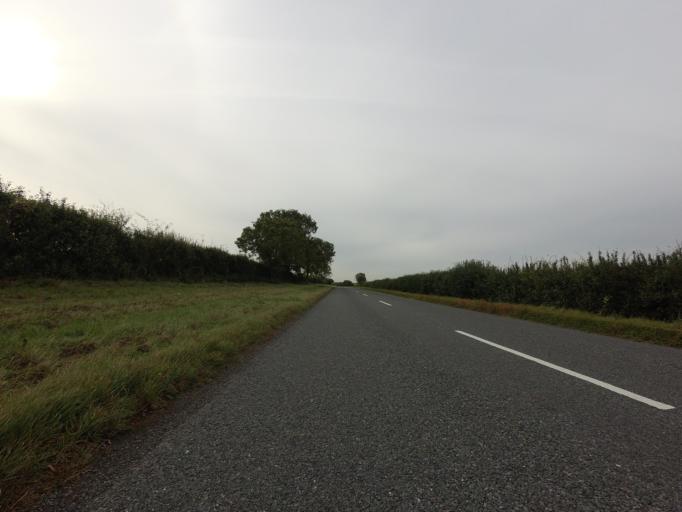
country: GB
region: England
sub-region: Cambridgeshire
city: Melbourn
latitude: 52.0485
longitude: 0.0459
